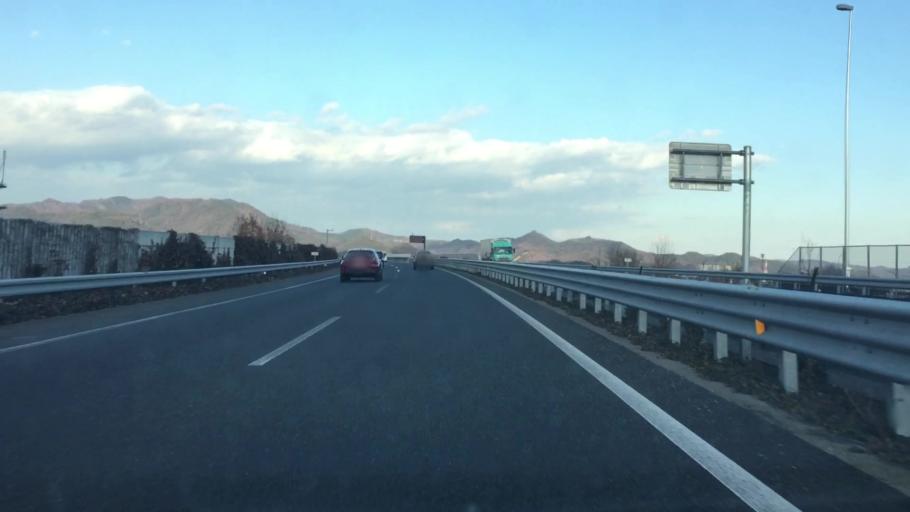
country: JP
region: Gunma
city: Ota
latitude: 36.3318
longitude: 139.3924
